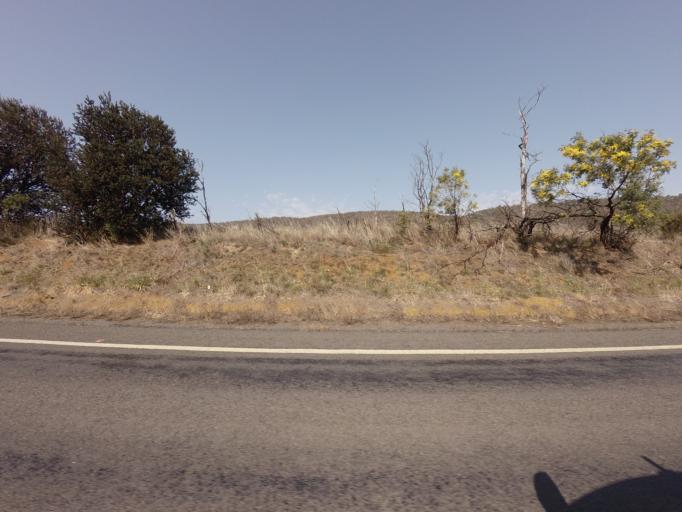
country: AU
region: Tasmania
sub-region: Northern Midlands
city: Evandale
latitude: -41.8122
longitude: 147.6137
